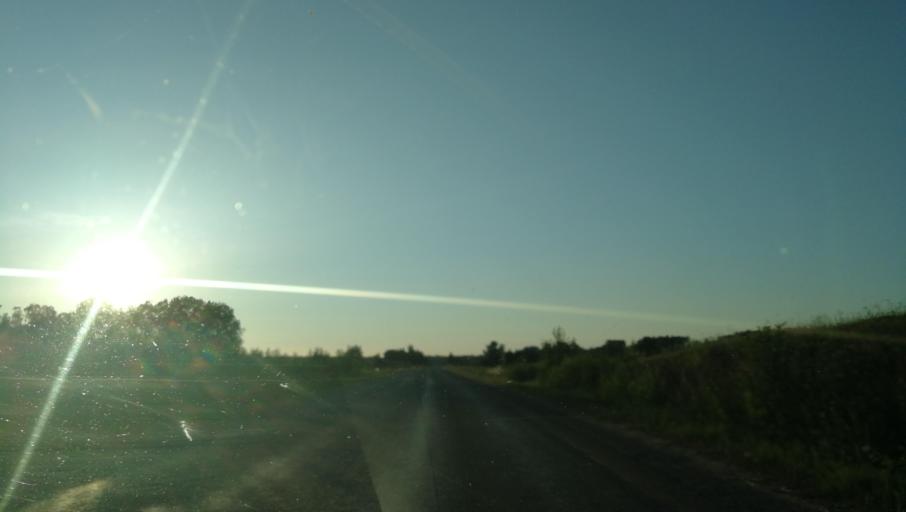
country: LV
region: Priekuli
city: Priekuli
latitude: 57.2772
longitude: 25.3222
